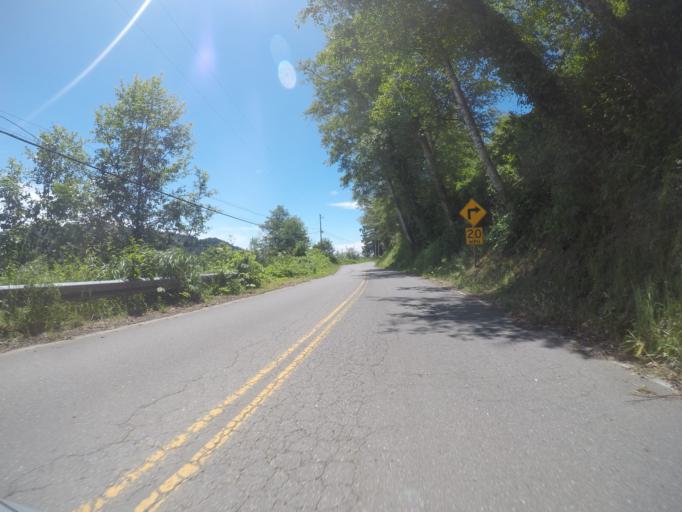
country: US
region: California
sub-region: Del Norte County
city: Bertsch-Oceanview
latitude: 41.5480
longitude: -124.0732
